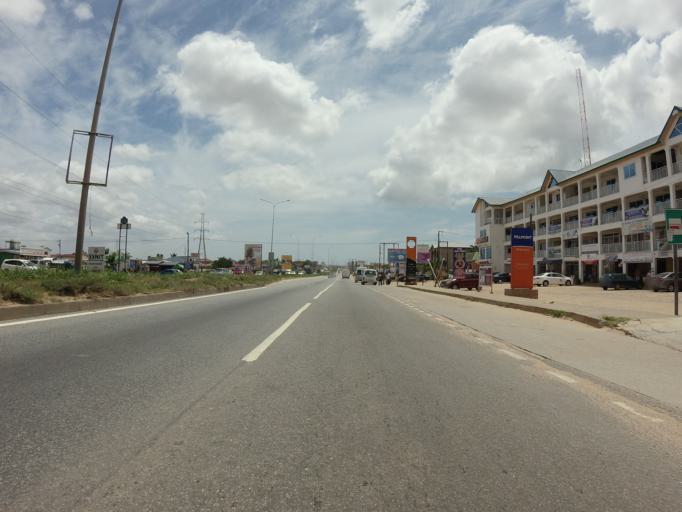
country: GH
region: Greater Accra
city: Gbawe
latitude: 5.5497
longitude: -0.3532
